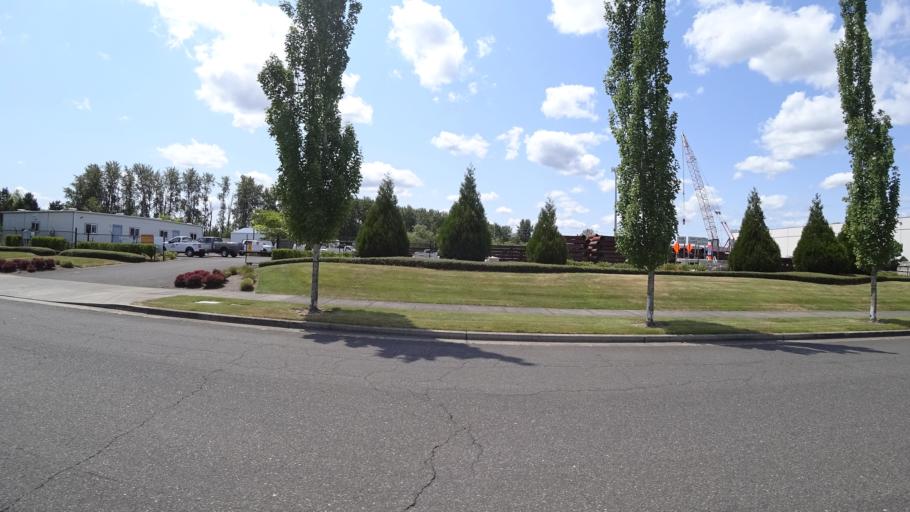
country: US
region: Washington
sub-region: Clark County
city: Lake Shore
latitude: 45.6301
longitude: -122.7518
